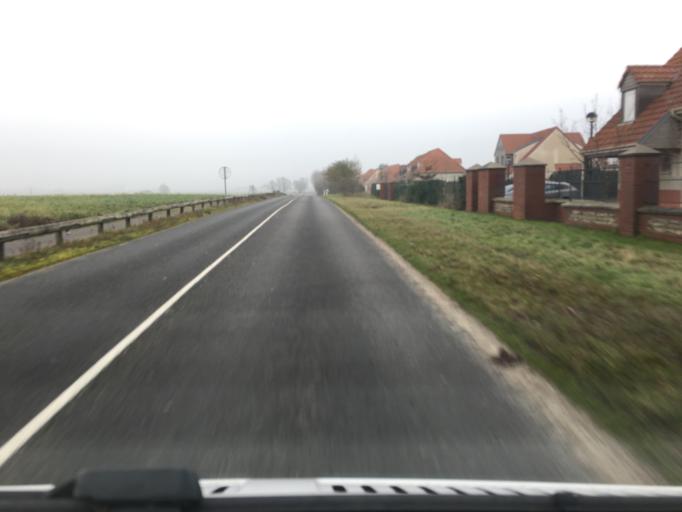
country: FR
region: Picardie
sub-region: Departement de la Somme
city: Le Crotoy
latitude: 50.2282
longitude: 1.6163
